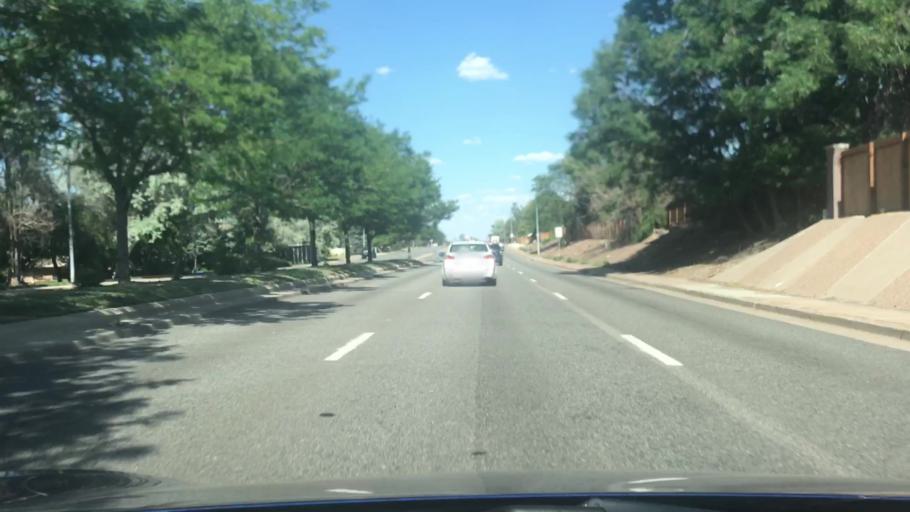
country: US
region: Colorado
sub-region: Arapahoe County
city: Dove Valley
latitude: 39.6530
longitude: -104.8186
